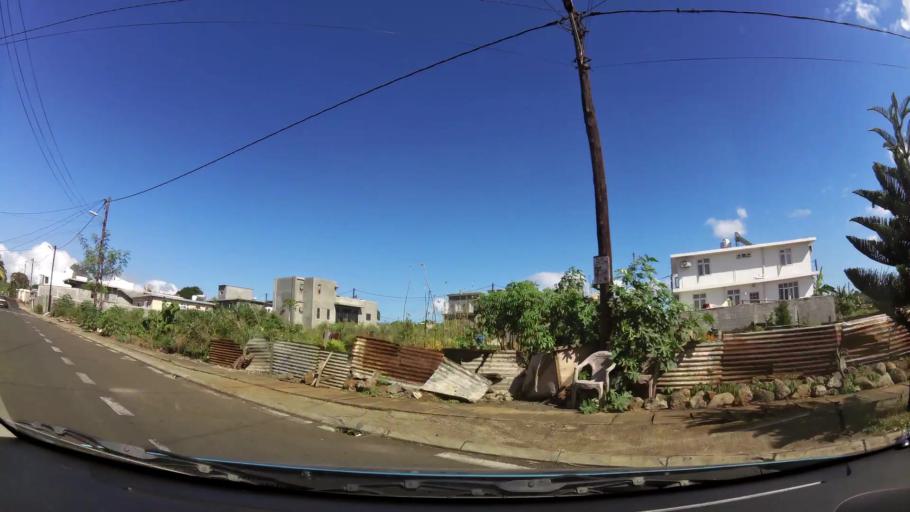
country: MU
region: Black River
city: Gros Cailloux
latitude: -20.2206
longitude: 57.4279
